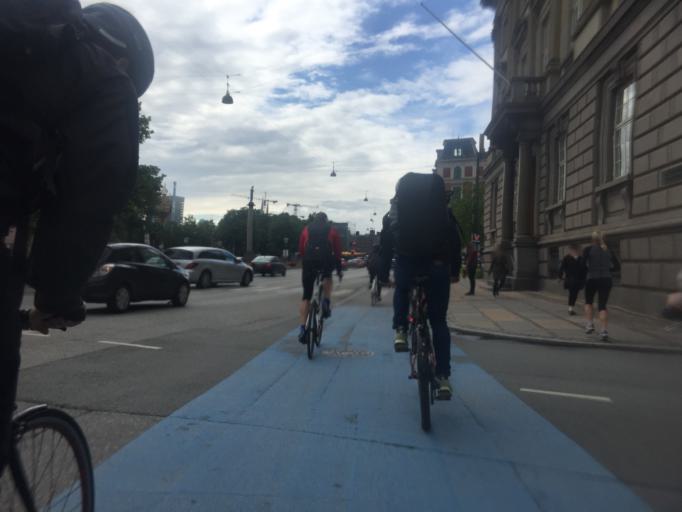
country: DK
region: Capital Region
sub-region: Kobenhavn
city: Copenhagen
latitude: 55.6729
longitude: 12.5741
